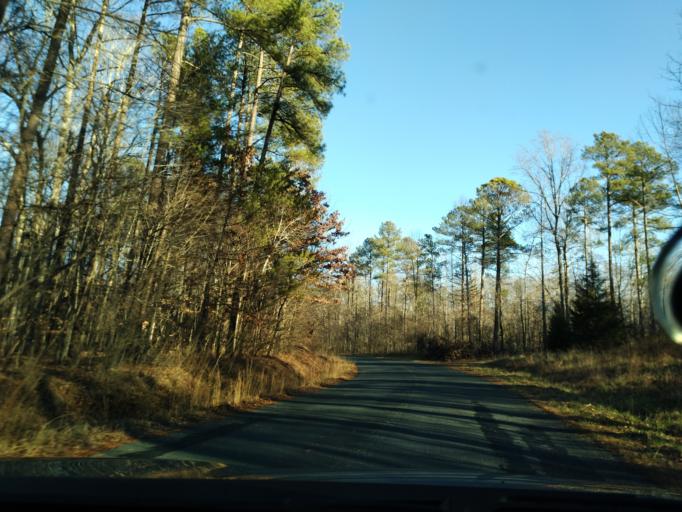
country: US
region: Virginia
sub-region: Appomattox County
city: Appomattox
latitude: 37.3823
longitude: -78.6462
